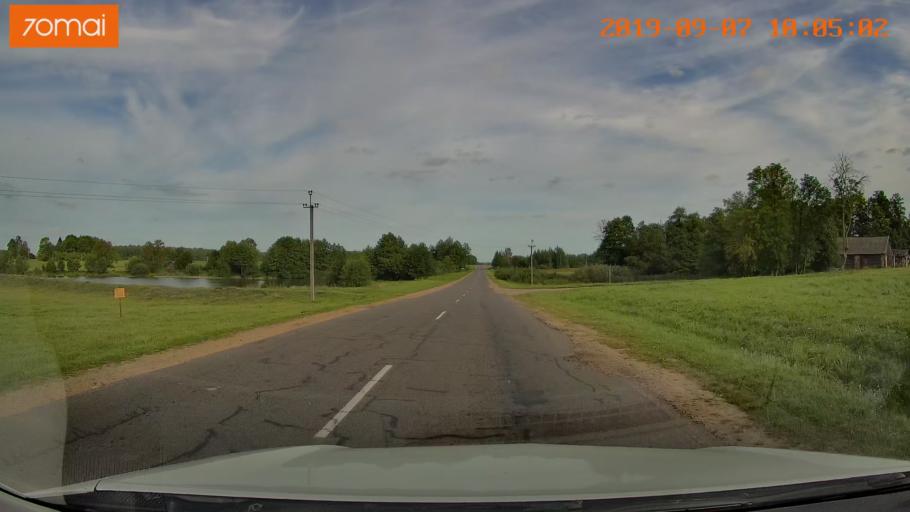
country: BY
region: Grodnenskaya
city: Voranava
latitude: 54.0423
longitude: 25.4093
